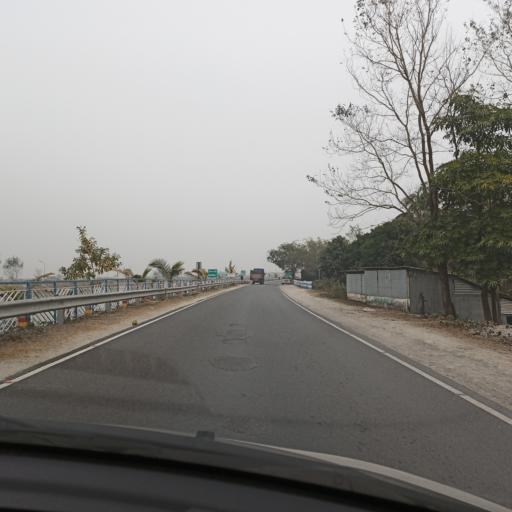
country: IN
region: West Bengal
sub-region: Jalpaiguri
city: Odlabari
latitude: 26.7383
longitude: 88.5753
